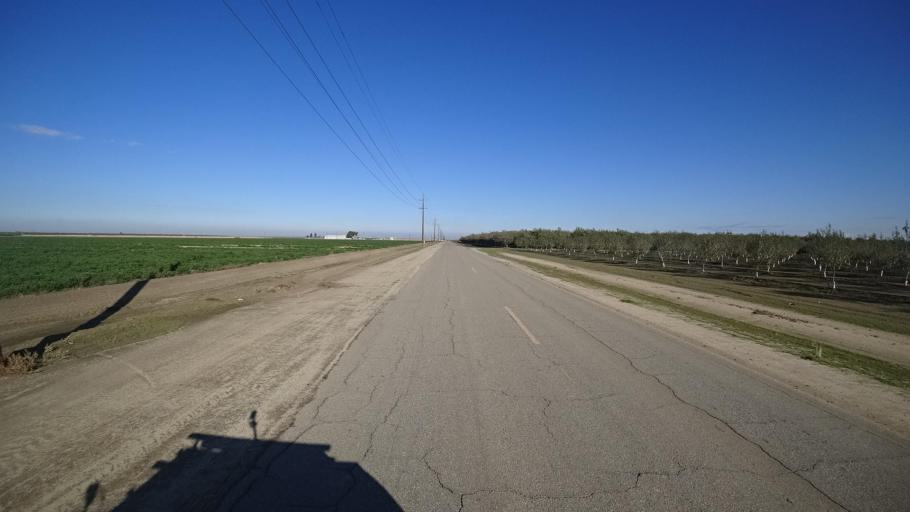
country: US
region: California
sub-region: Kern County
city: McFarland
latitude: 35.6771
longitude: -119.2765
